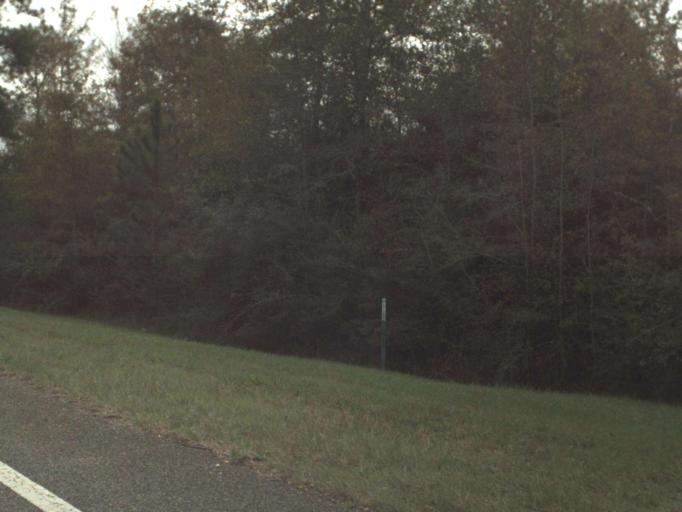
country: US
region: Florida
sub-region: Escambia County
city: Cantonment
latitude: 30.6484
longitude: -87.3503
